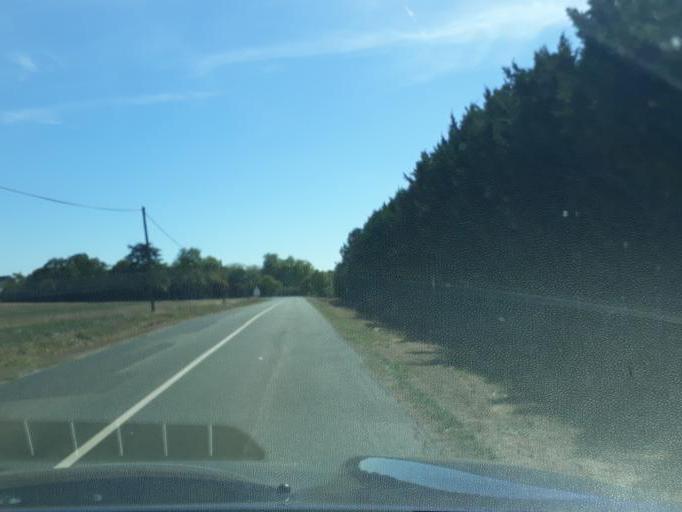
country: FR
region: Centre
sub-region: Departement du Loir-et-Cher
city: Ouzouer-le-Marche
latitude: 47.9217
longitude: 1.5210
